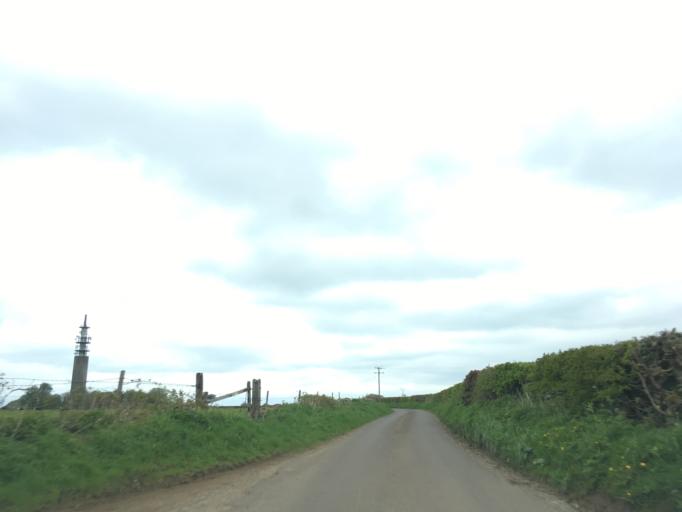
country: GB
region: England
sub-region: Gloucestershire
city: Wotton-under-Edge
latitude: 51.6450
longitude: -2.3051
